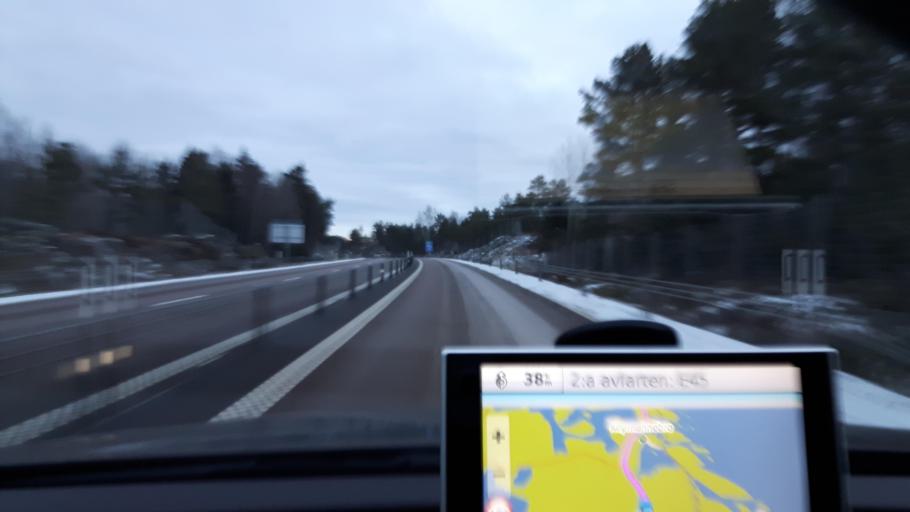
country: SE
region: Vaestra Goetaland
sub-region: Melleruds Kommun
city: Mellerud
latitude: 58.7547
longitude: 12.4884
